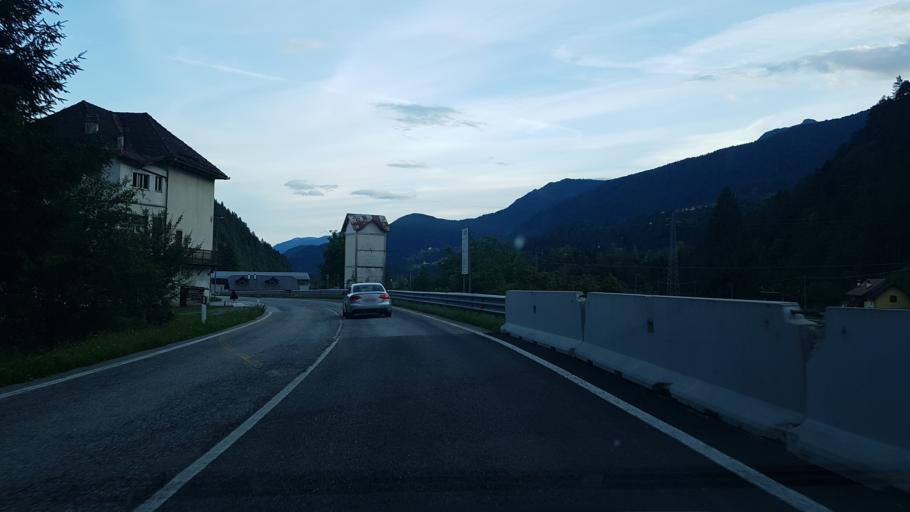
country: IT
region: Friuli Venezia Giulia
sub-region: Provincia di Udine
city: Comeglians
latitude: 46.5170
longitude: 12.8652
